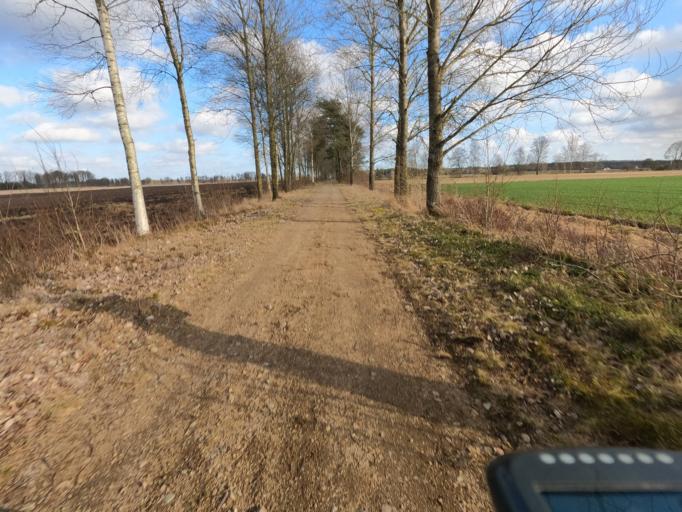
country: SE
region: Kronoberg
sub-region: Alvesta Kommun
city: Vislanda
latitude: 56.7303
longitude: 14.5594
